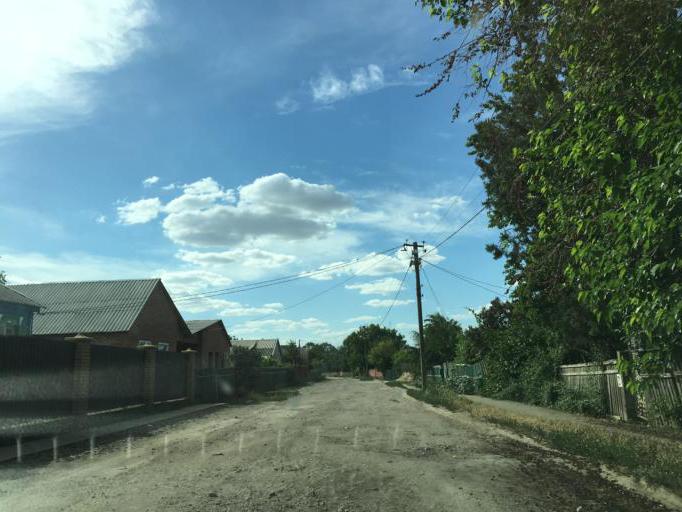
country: RU
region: Krasnodarskiy
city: Kushchevskaya
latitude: 46.5646
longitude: 39.6427
